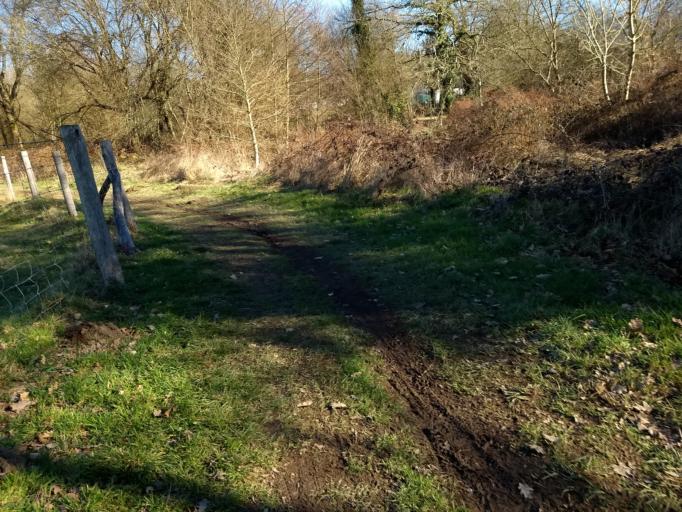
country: FR
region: Limousin
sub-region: Departement de la Haute-Vienne
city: Isle
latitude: 45.8230
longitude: 1.2099
